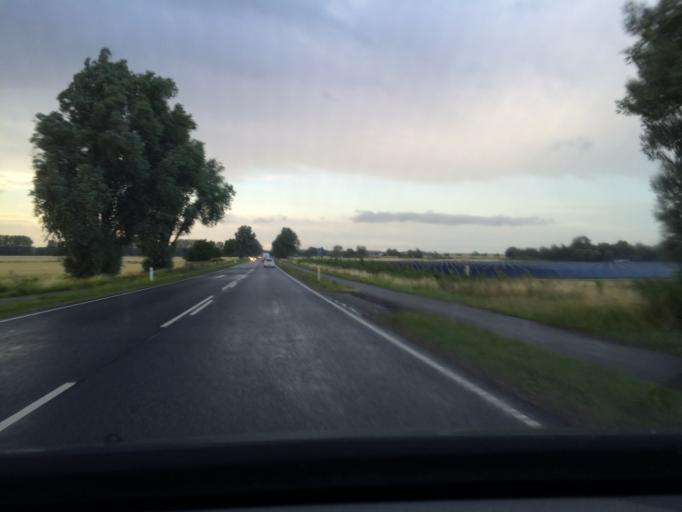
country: DK
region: Zealand
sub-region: Guldborgsund Kommune
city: Nykobing Falster
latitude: 54.7161
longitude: 11.9207
